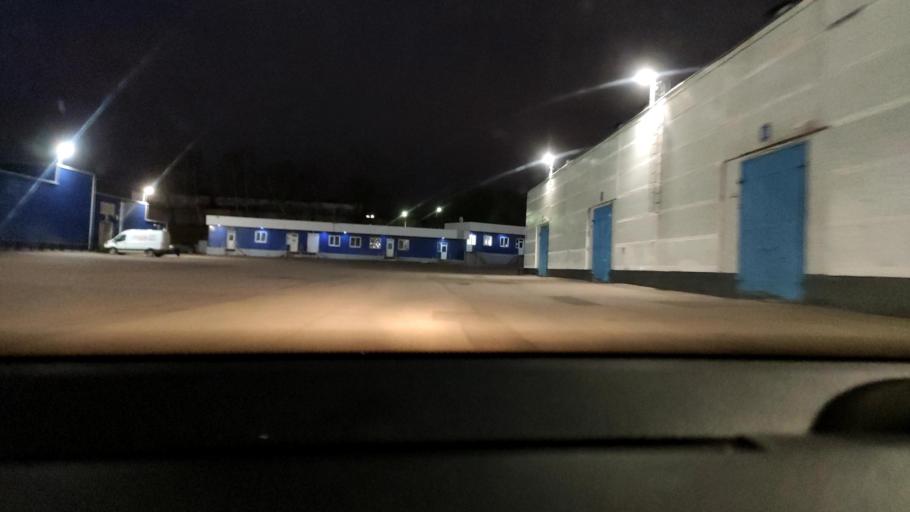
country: RU
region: Moskovskaya
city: Biryulevo Zapadnoye
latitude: 55.5924
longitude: 37.6243
